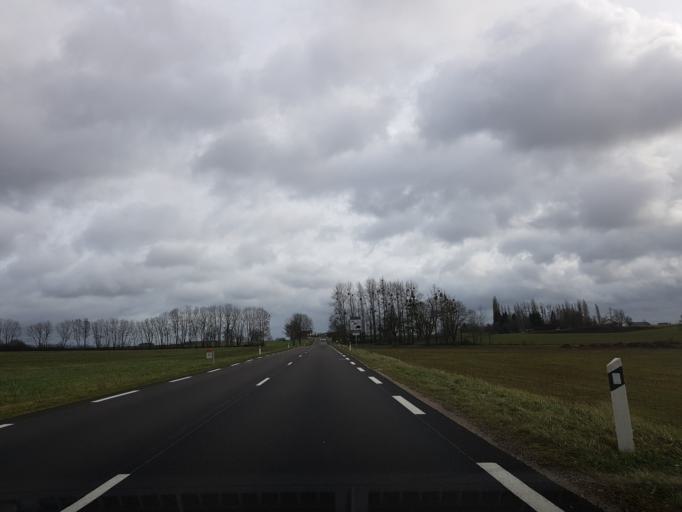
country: FR
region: Champagne-Ardenne
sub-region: Departement de la Haute-Marne
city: Chalindrey
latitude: 47.8521
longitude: 5.4072
